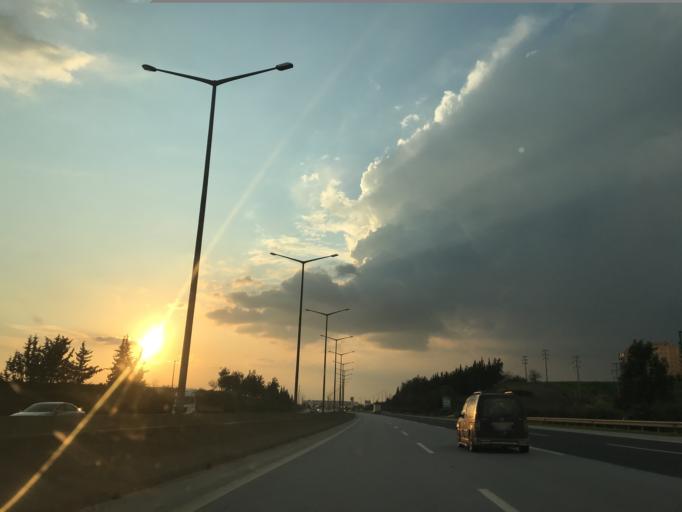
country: TR
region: Adana
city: Seyhan
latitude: 37.0297
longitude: 35.2154
